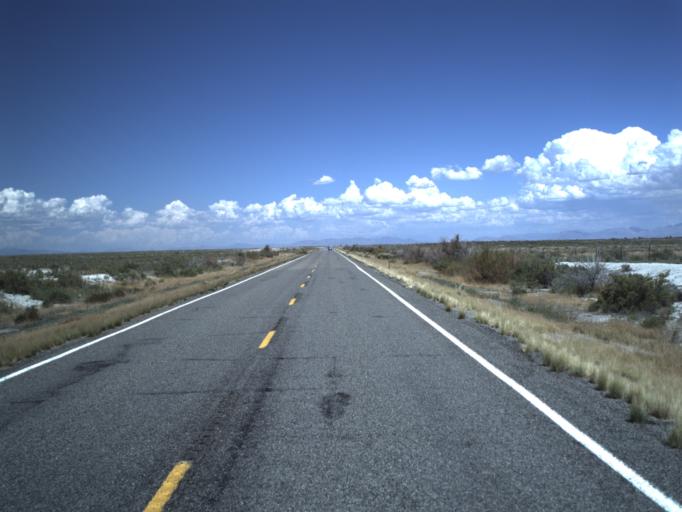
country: US
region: Utah
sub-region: Millard County
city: Delta
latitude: 39.2988
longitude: -112.8139
